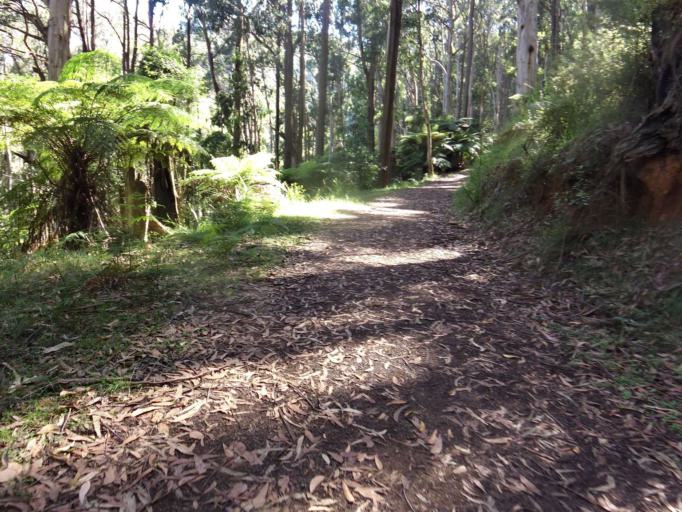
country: AU
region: Victoria
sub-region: Yarra Ranges
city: Olinda
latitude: -37.8456
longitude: 145.3501
